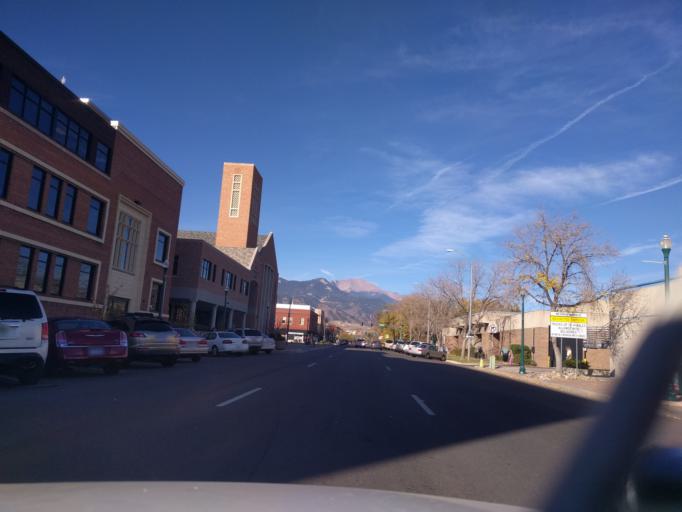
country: US
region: Colorado
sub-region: El Paso County
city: Colorado Springs
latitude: 38.8366
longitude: -104.8201
